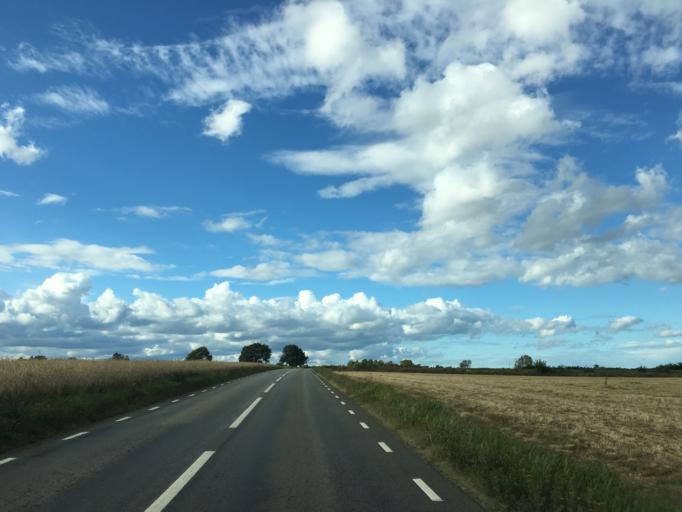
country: SE
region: Kalmar
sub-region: Morbylanga Kommun
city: Moerbylanga
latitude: 56.4675
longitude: 16.4293
